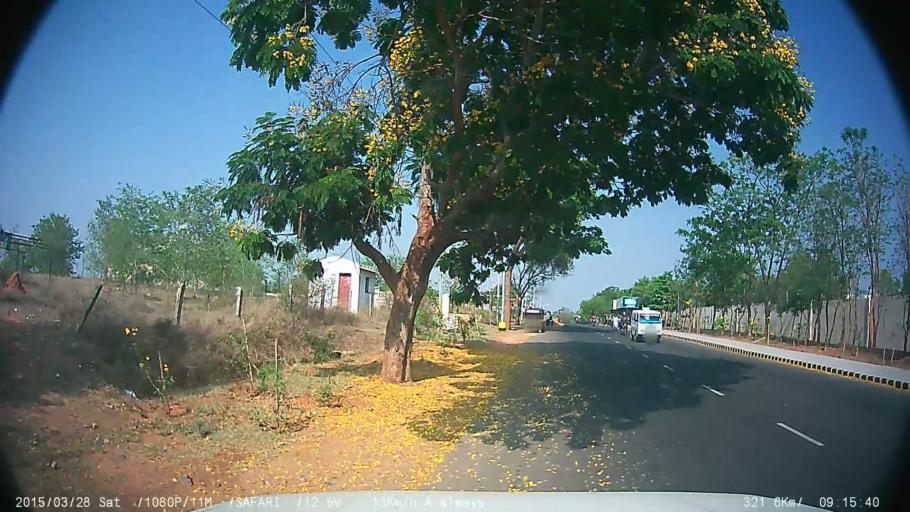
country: IN
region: Karnataka
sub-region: Mysore
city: Mysore
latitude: 12.3578
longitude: 76.6025
